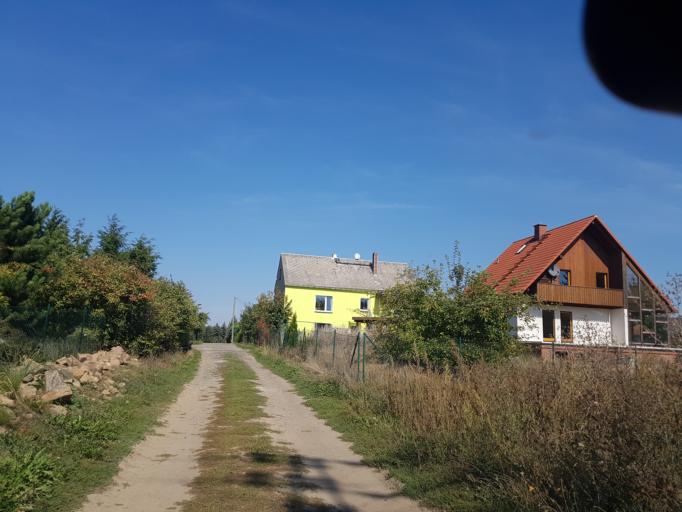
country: DE
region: Saxony
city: Kriebstein
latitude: 51.0566
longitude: 13.0092
